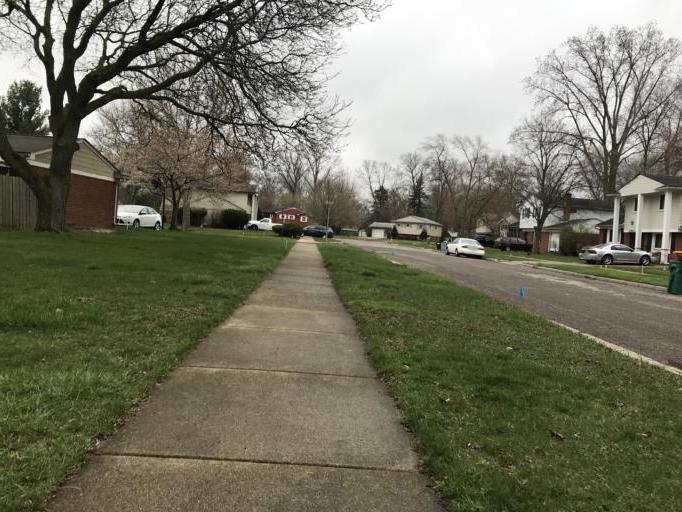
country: US
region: Michigan
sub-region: Oakland County
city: Farmington
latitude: 42.4683
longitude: -83.3441
